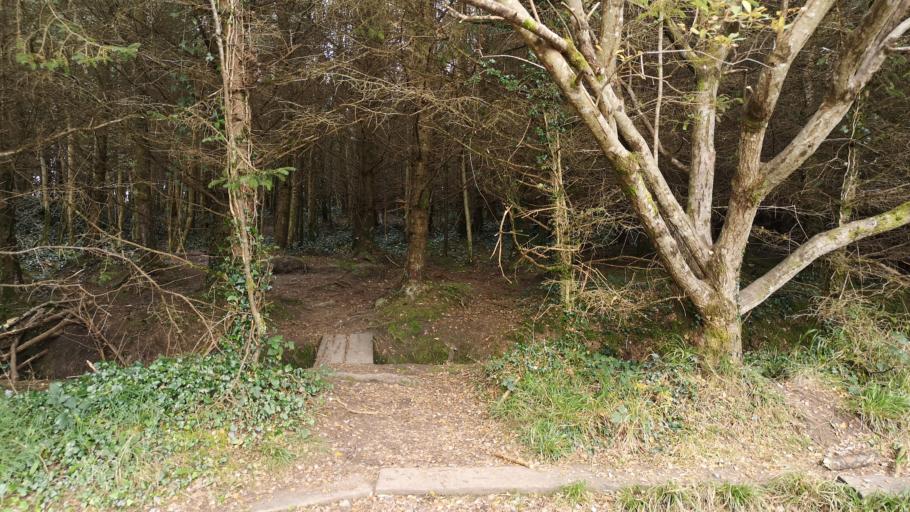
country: IE
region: Connaught
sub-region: County Galway
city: Loughrea
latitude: 53.2391
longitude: -8.6508
